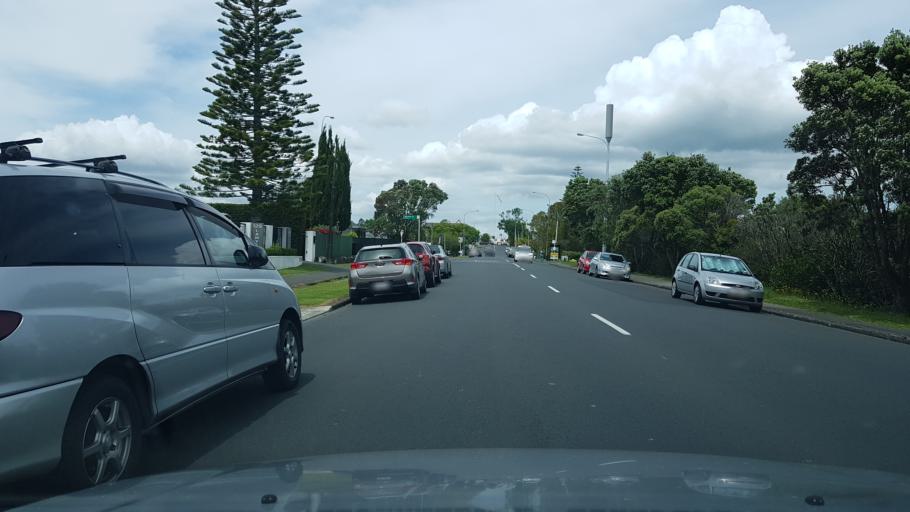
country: NZ
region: Auckland
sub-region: Auckland
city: North Shore
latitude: -36.8062
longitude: 174.7254
